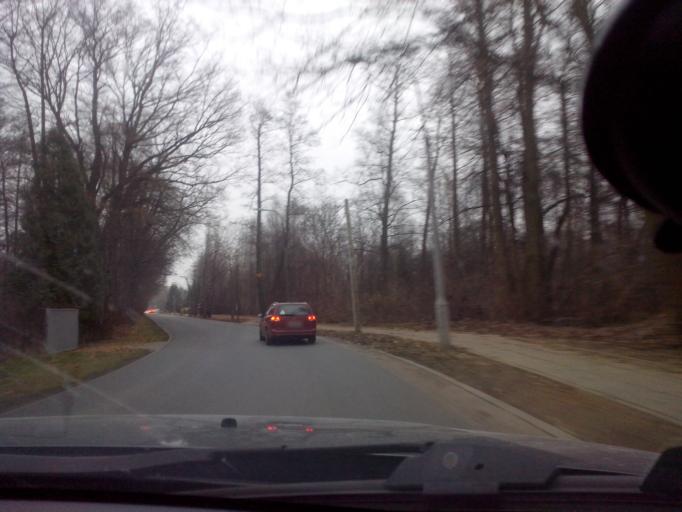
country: PL
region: Masovian Voivodeship
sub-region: Warszawa
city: Bialoleka
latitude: 52.3497
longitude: 20.9719
